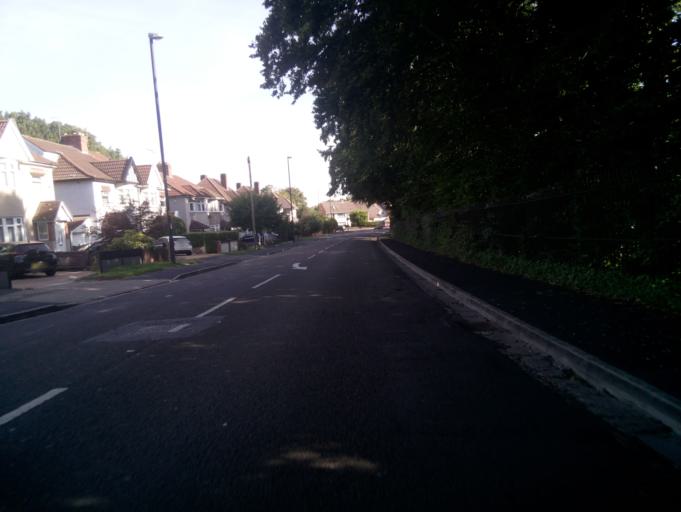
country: GB
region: England
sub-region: Bath and North East Somerset
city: Whitchurch
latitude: 51.4252
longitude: -2.5571
